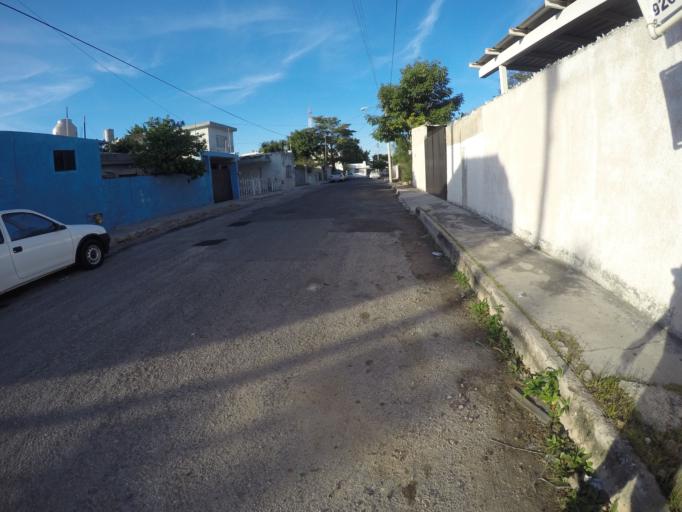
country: MX
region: Yucatan
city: Merida
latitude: 20.9824
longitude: -89.6154
